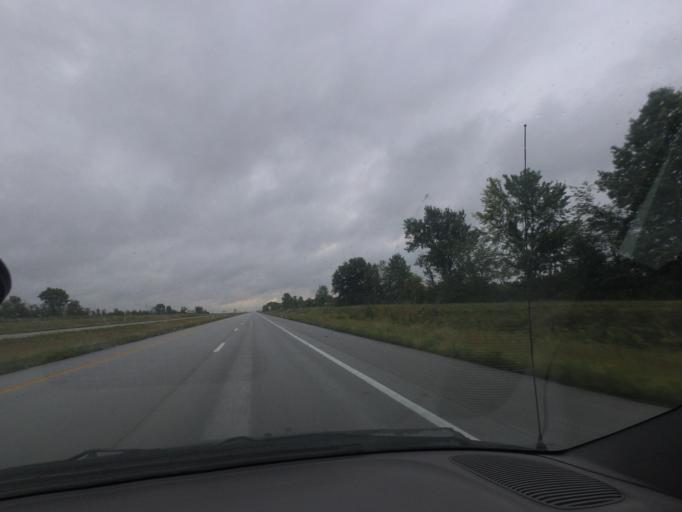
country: US
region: Missouri
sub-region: Marion County
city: Monroe City
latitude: 39.6637
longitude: -91.7048
